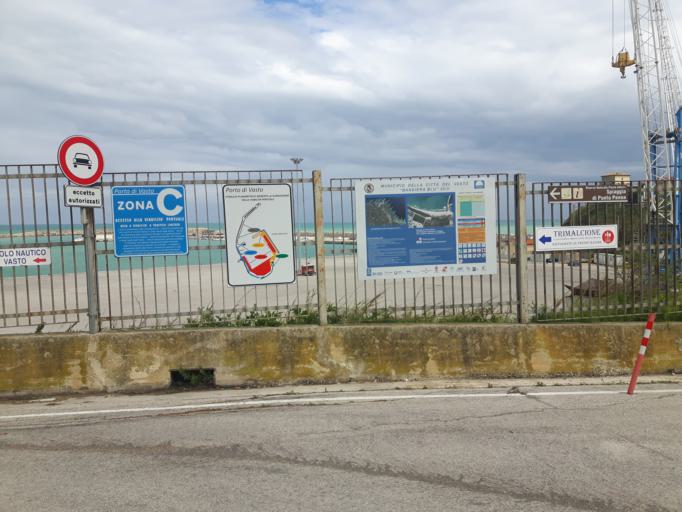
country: IT
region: Abruzzo
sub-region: Provincia di Chieti
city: Vasto
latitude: 42.1711
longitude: 14.7123
